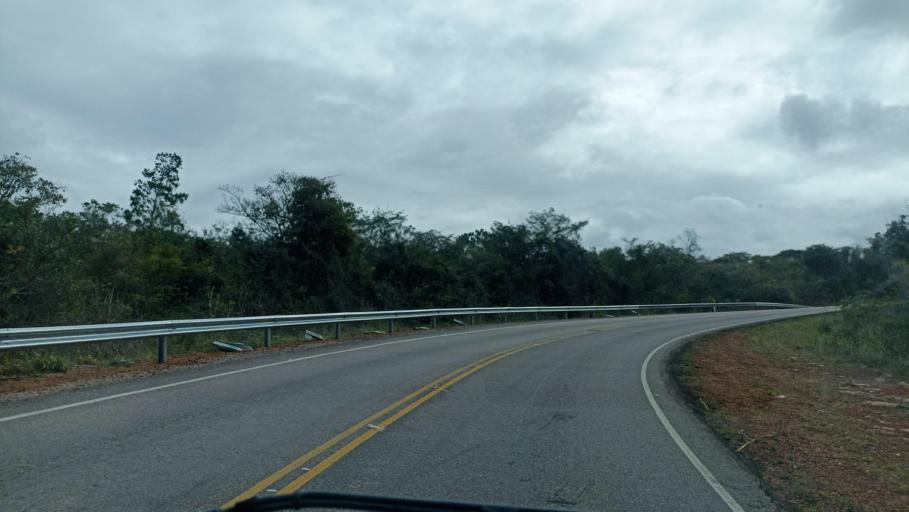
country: BR
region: Bahia
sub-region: Andarai
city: Vera Cruz
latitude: -12.9334
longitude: -41.2415
